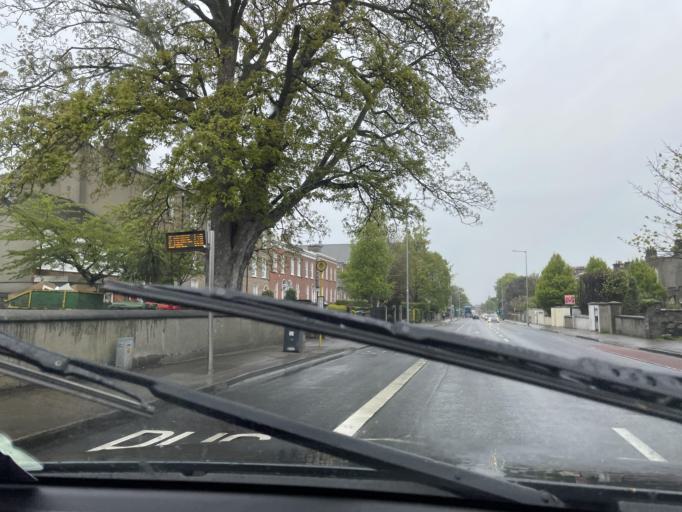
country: IE
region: Leinster
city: Rathgar
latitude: 53.3158
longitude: -6.2715
